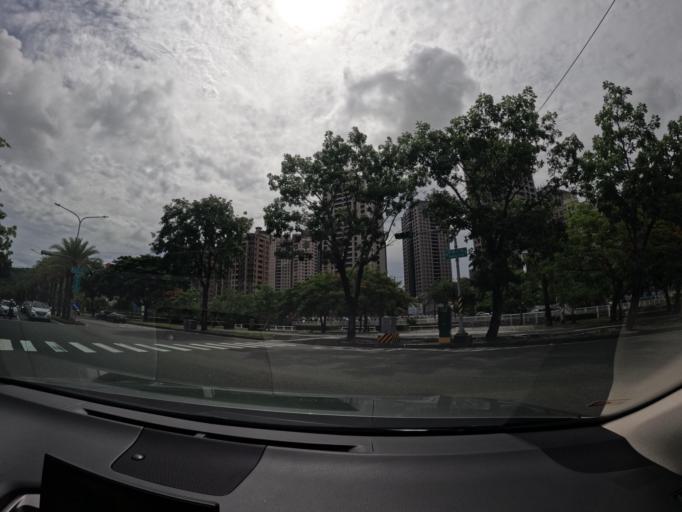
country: TW
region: Kaohsiung
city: Kaohsiung
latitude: 22.6488
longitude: 120.2858
